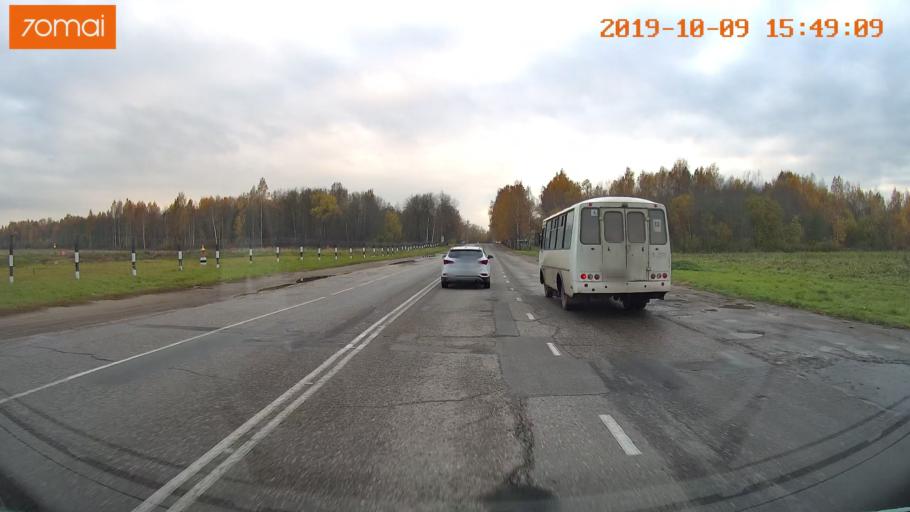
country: RU
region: Kostroma
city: Oktyabr'skiy
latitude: 57.8070
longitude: 41.0081
